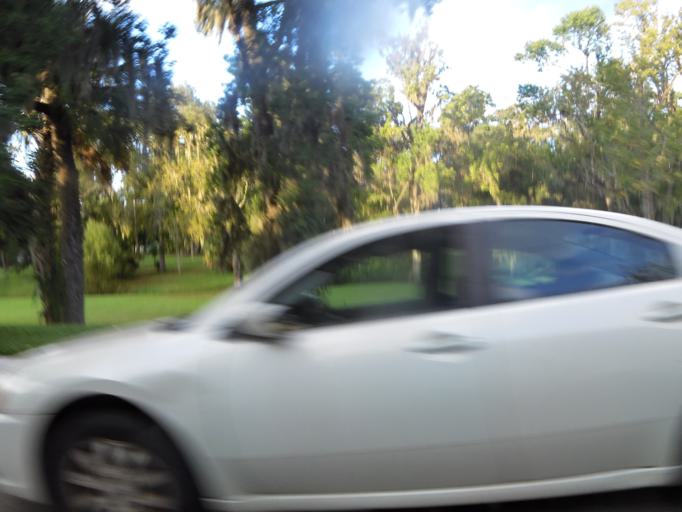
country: US
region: Florida
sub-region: Duval County
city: Jacksonville
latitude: 30.3066
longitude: -81.7005
